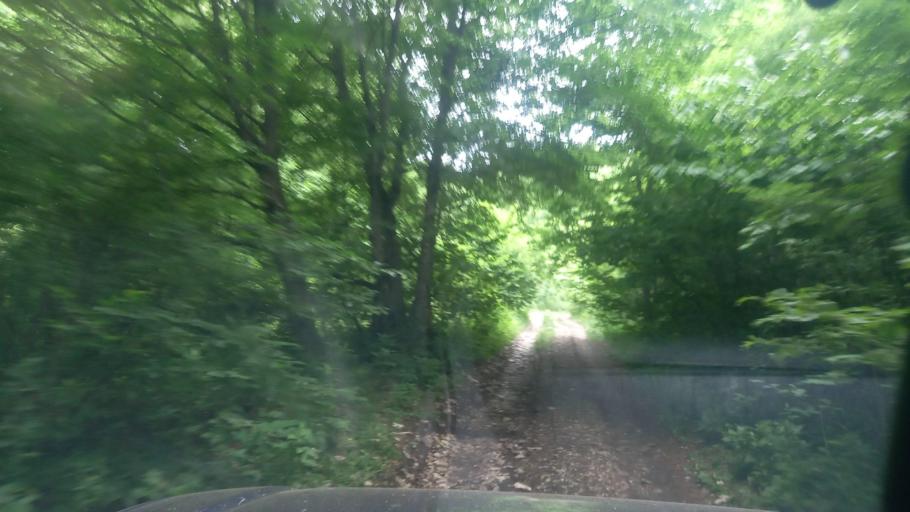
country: RU
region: Karachayevo-Cherkesiya
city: Pregradnaya
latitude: 44.0254
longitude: 41.2985
